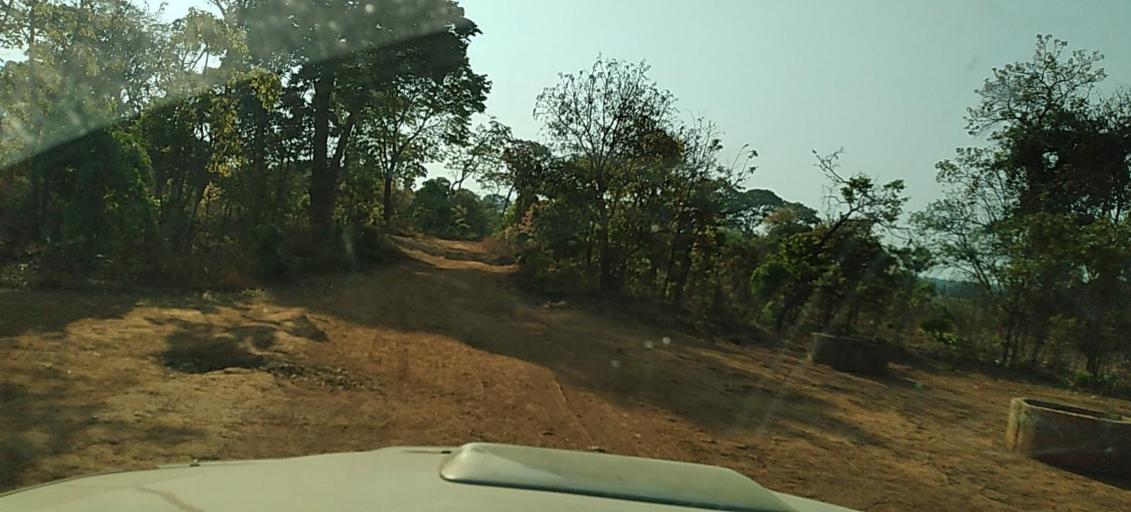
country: ZM
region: North-Western
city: Kasempa
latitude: -13.1841
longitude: 25.9540
